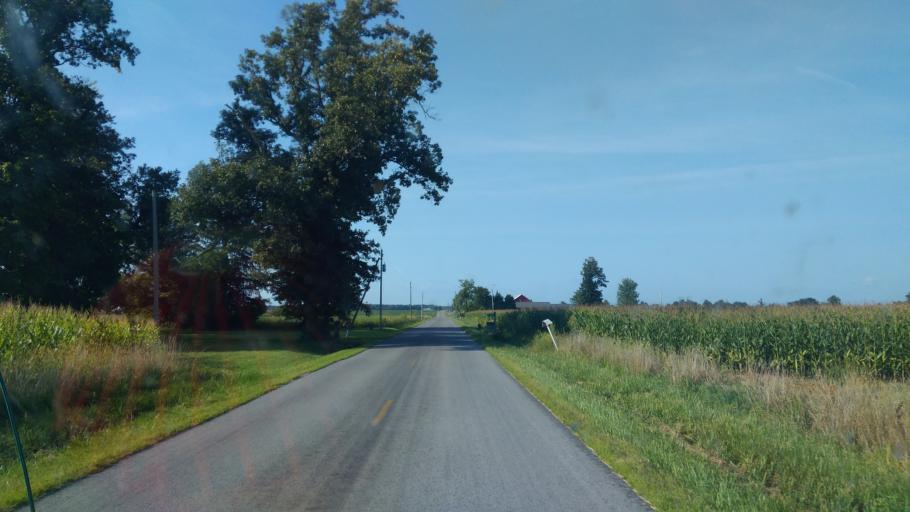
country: US
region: Ohio
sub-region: Hardin County
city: Forest
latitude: 40.8447
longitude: -83.4189
